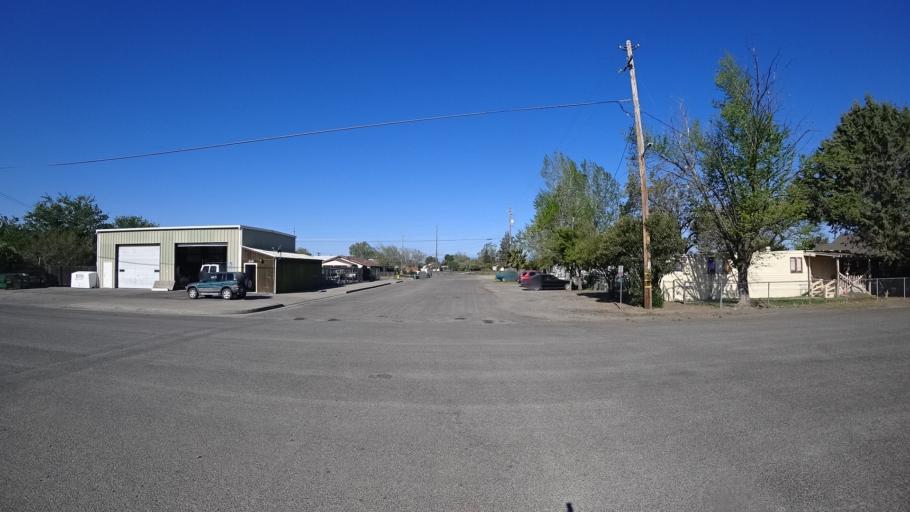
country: US
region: California
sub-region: Glenn County
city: Orland
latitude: 39.7532
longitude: -122.1954
